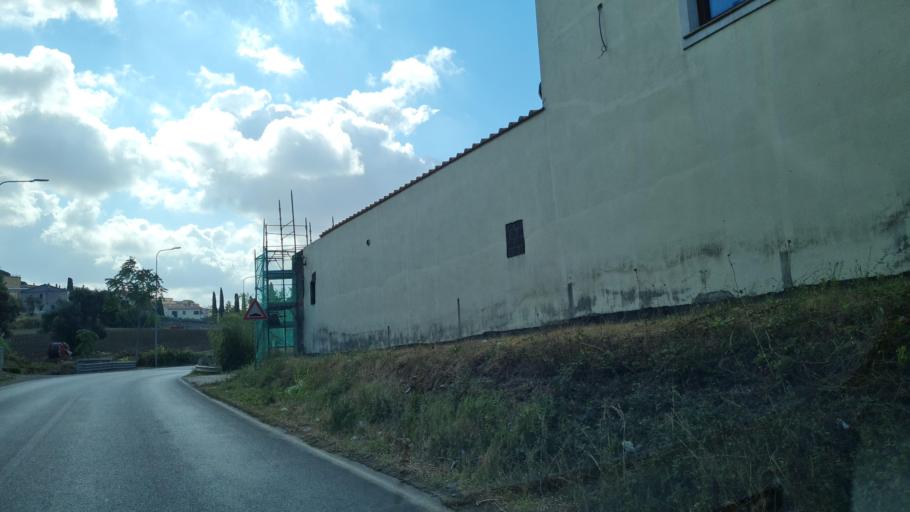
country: IT
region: Latium
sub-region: Provincia di Viterbo
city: Tarquinia
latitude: 42.2524
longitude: 11.7488
